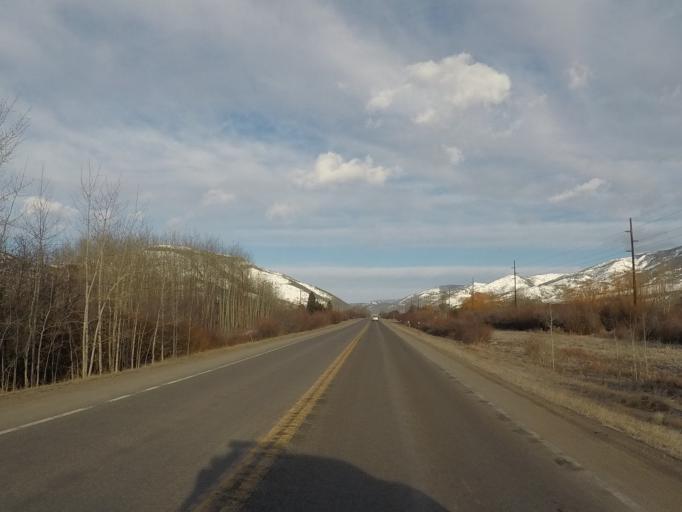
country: US
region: Montana
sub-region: Deer Lodge County
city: Anaconda
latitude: 46.1431
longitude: -112.9947
